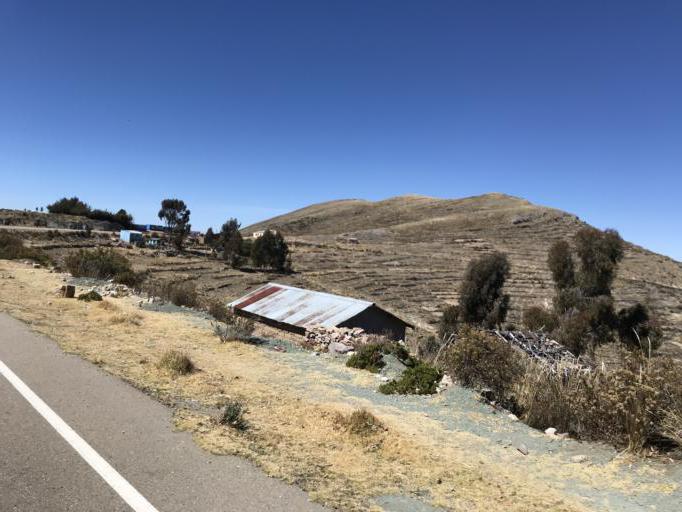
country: BO
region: La Paz
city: San Pedro
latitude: -16.2002
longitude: -68.9055
